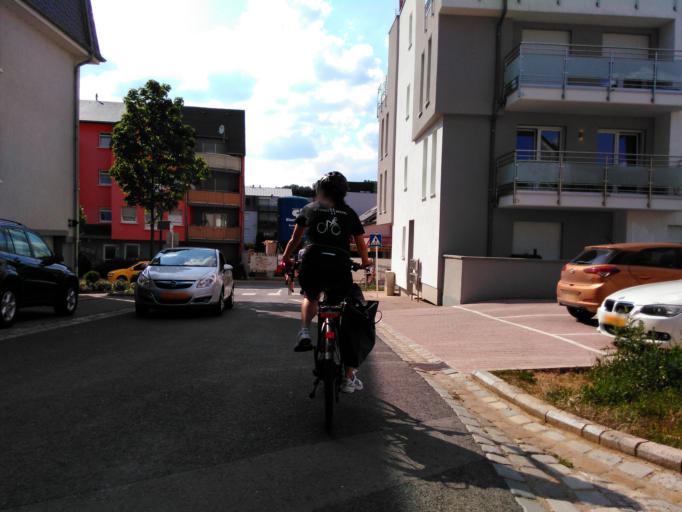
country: LU
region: Luxembourg
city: Tetange
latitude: 49.4732
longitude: 6.0404
